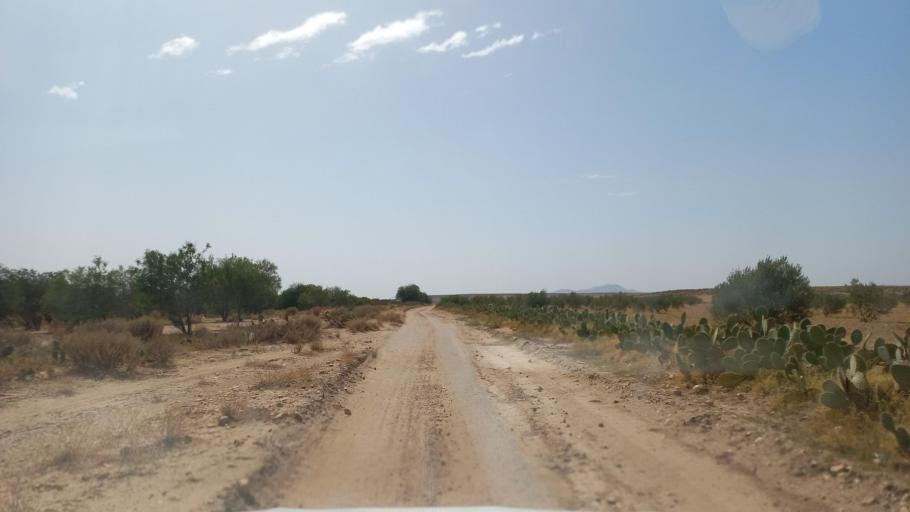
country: TN
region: Al Qasrayn
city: Kasserine
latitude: 35.2545
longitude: 8.9599
